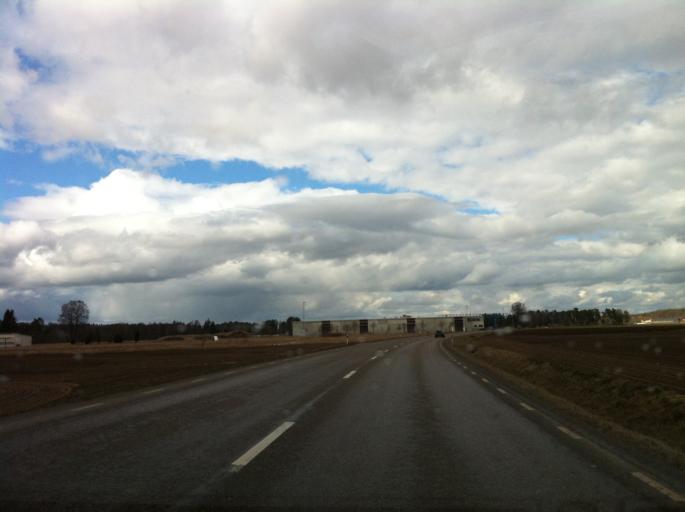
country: SE
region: Vaestra Goetaland
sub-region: Ulricehamns Kommun
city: Ulricehamn
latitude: 57.7632
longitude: 13.4055
